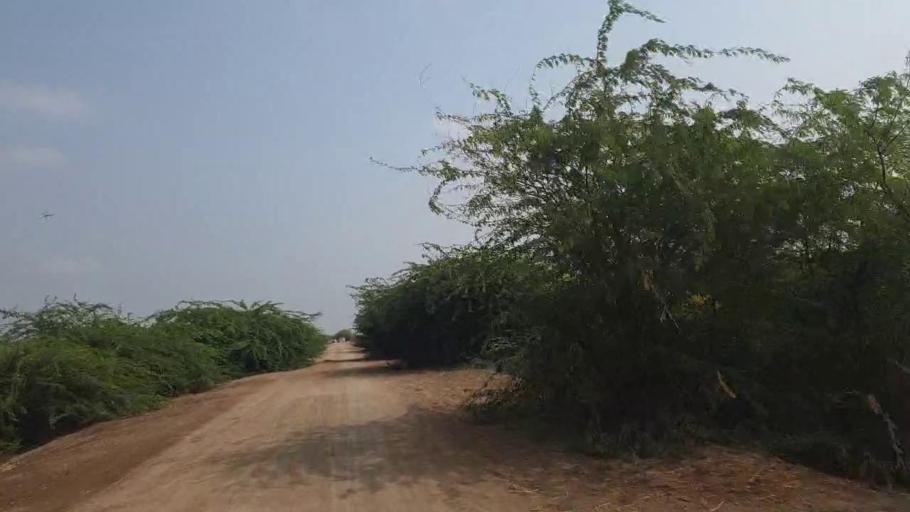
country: PK
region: Sindh
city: Badin
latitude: 24.5475
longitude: 68.7166
